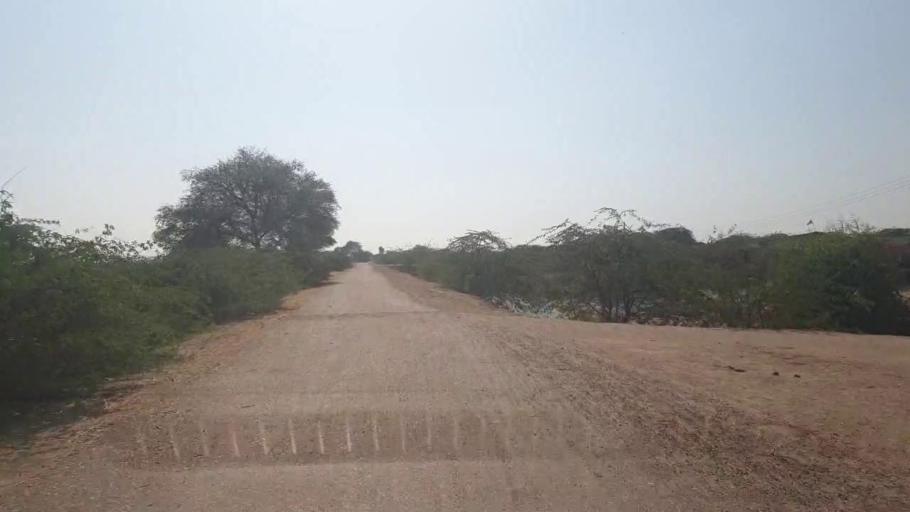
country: PK
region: Sindh
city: Badin
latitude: 24.5531
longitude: 68.8146
